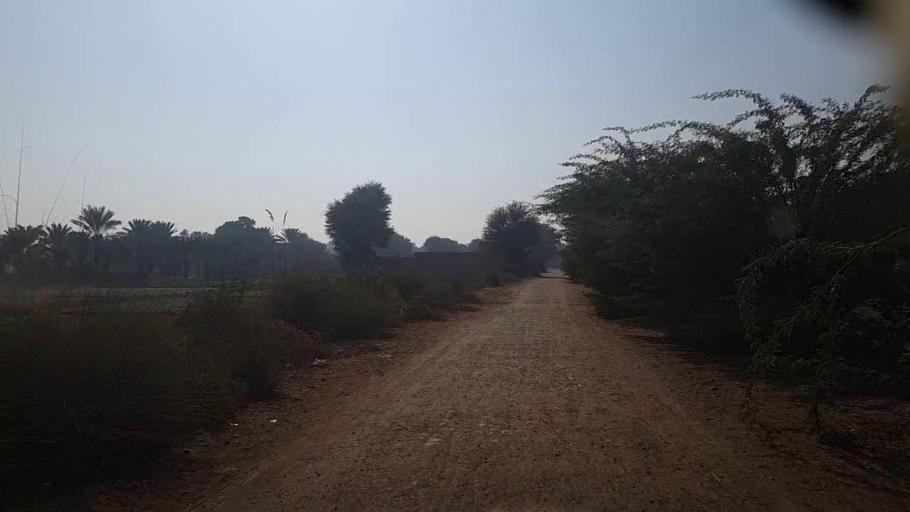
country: PK
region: Sindh
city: Kandiari
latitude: 27.0269
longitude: 68.5058
